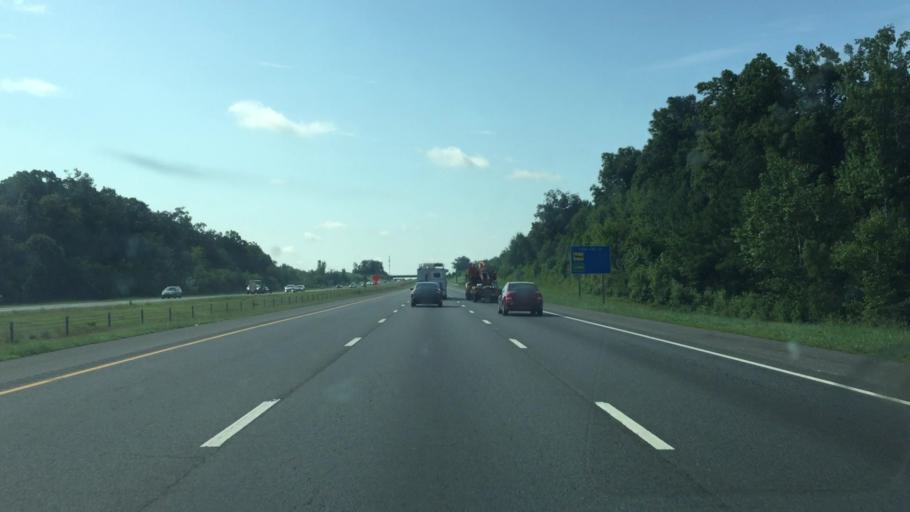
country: US
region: North Carolina
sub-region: Cabarrus County
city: Harrisburg
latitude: 35.2933
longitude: -80.6811
